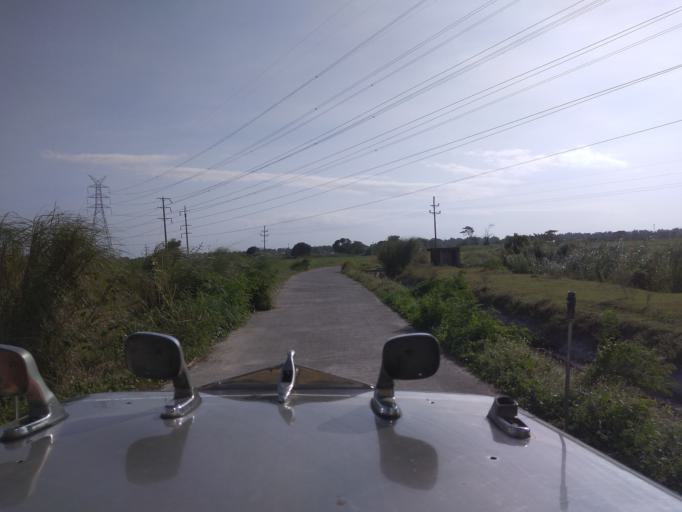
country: PH
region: Central Luzon
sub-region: Province of Pampanga
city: San Patricio
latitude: 15.1026
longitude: 120.7023
